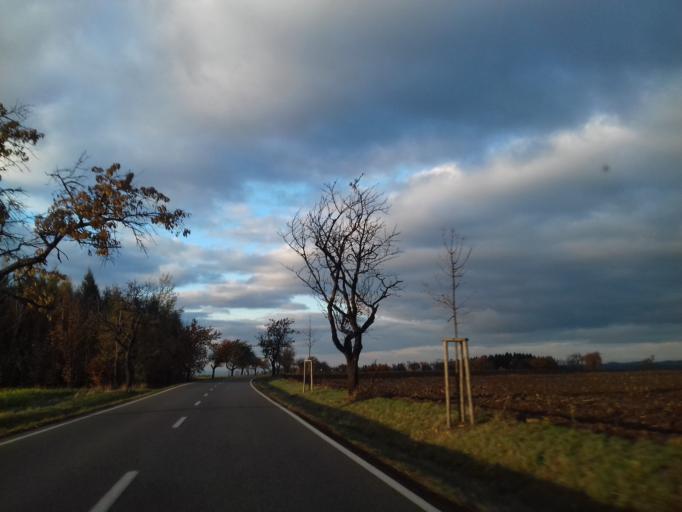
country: CZ
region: Pardubicky
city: Krouna
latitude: 49.8082
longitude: 16.0434
